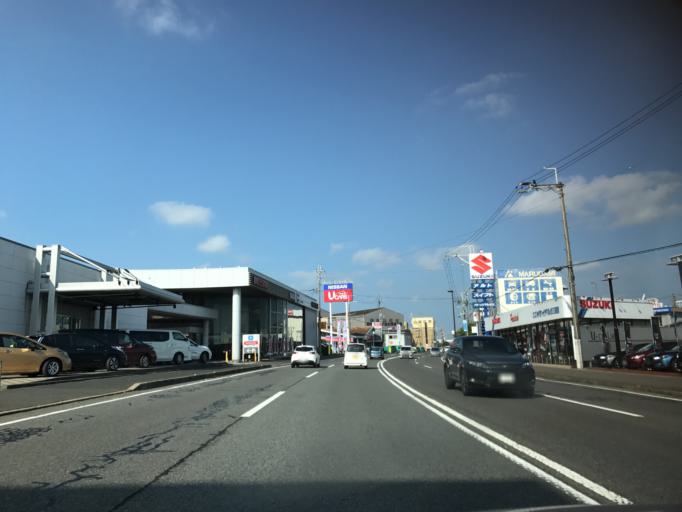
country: JP
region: Shiga Prefecture
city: Kusatsu
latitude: 35.0237
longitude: 135.9885
